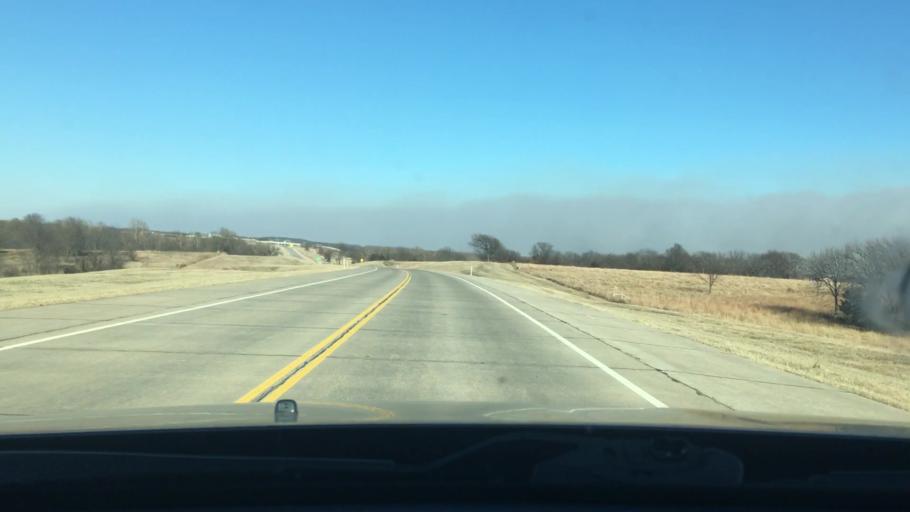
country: US
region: Oklahoma
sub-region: Murray County
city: Sulphur
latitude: 34.5521
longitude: -96.9435
